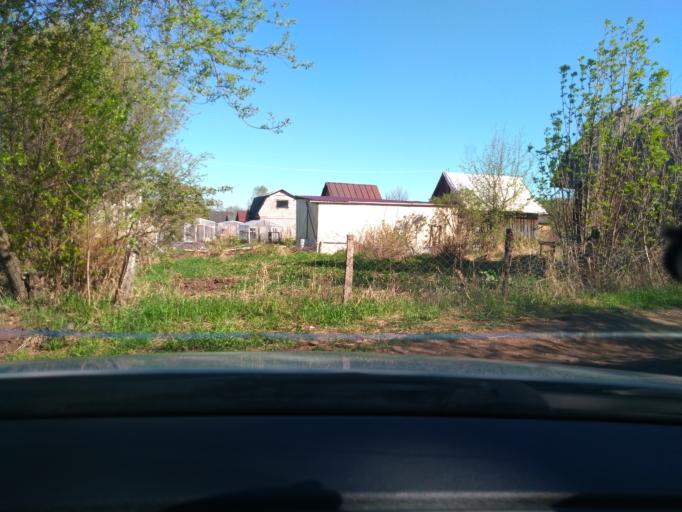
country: RU
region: Perm
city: Lobanovo
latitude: 57.8696
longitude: 56.3037
